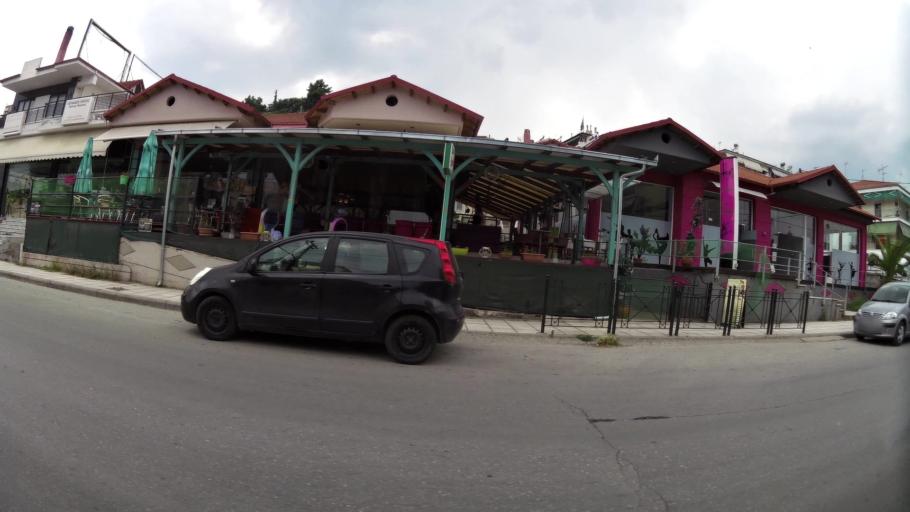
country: GR
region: Central Macedonia
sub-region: Nomos Imathias
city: Veroia
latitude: 40.5297
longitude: 22.2081
